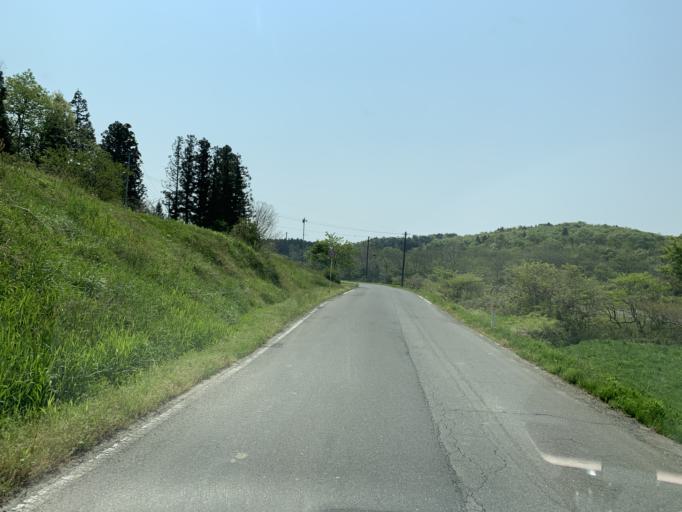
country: JP
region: Iwate
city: Ichinoseki
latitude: 38.8385
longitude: 141.0727
